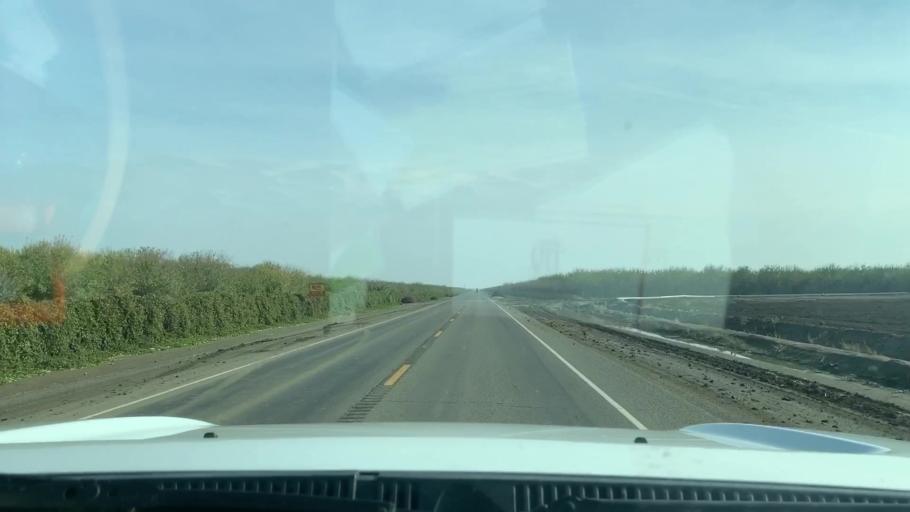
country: US
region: California
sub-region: Fresno County
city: Huron
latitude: 36.2552
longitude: -120.1410
